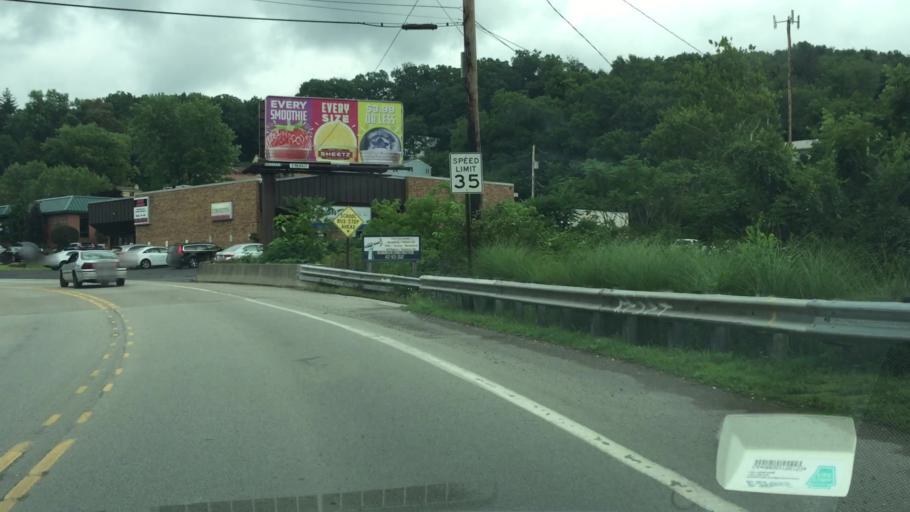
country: US
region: Pennsylvania
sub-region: Allegheny County
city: Millvale
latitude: 40.5066
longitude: -79.9894
